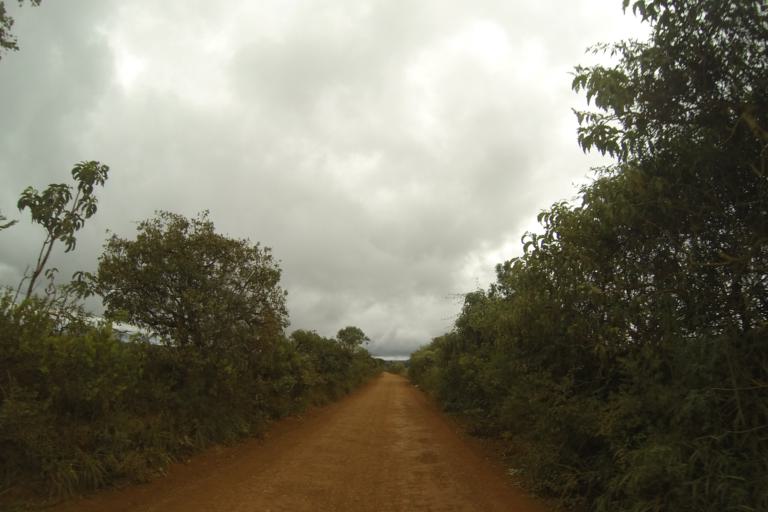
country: BR
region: Minas Gerais
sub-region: Campos Altos
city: Campos Altos
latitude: -19.7892
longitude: -46.3678
